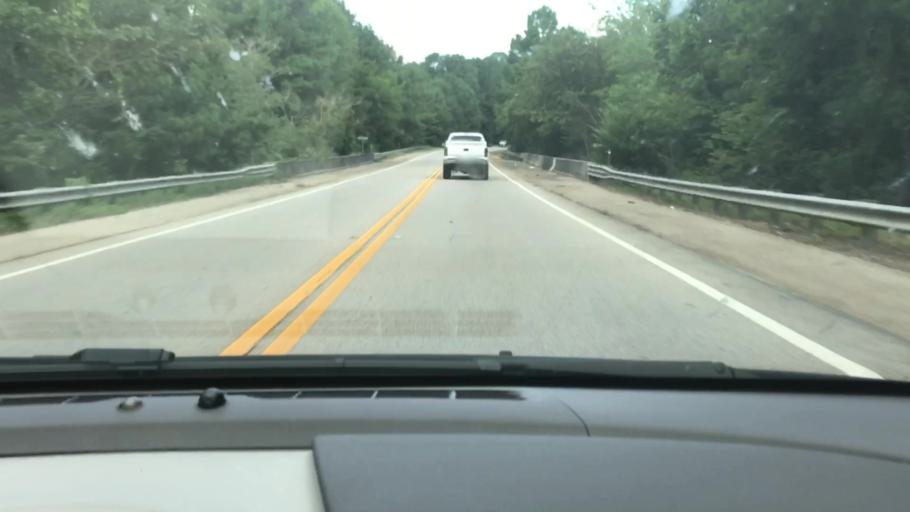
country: US
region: Georgia
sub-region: Troup County
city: La Grange
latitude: 32.9720
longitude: -85.0253
